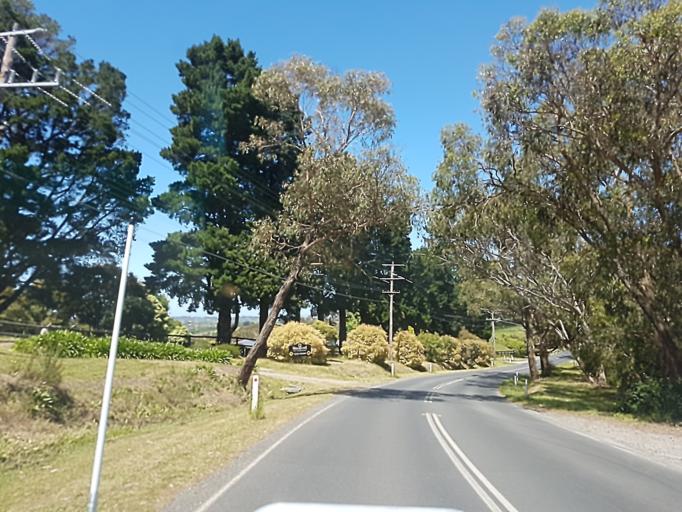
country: AU
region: Victoria
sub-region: Yarra Ranges
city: Selby
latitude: -37.9312
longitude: 145.3696
